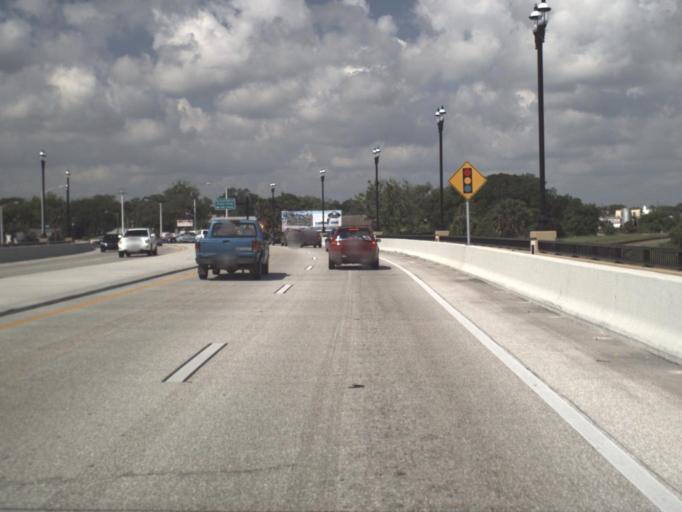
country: US
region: Florida
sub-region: Saint Johns County
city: Saint Augustine
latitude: 29.8927
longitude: -81.3231
